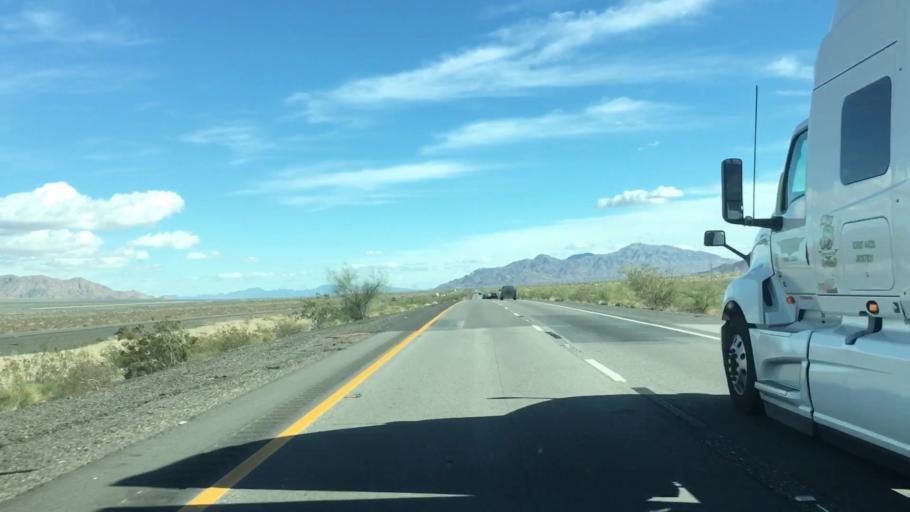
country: US
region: California
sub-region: Imperial County
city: Niland
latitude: 33.6692
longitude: -115.6386
